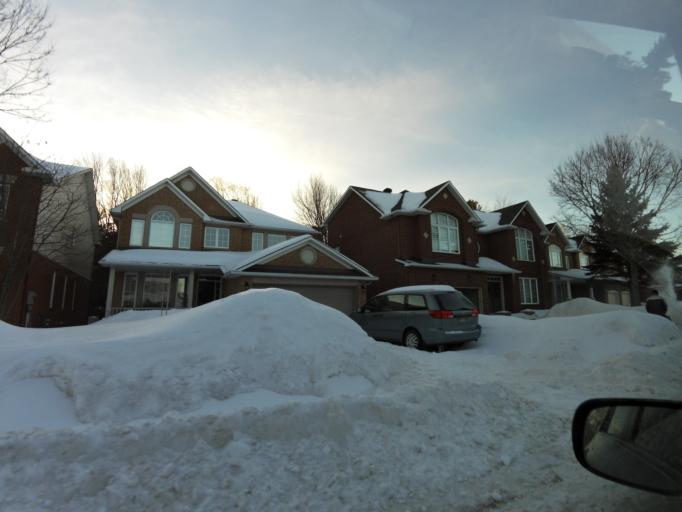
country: CA
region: Ontario
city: Ottawa
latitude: 45.4379
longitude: -75.5329
